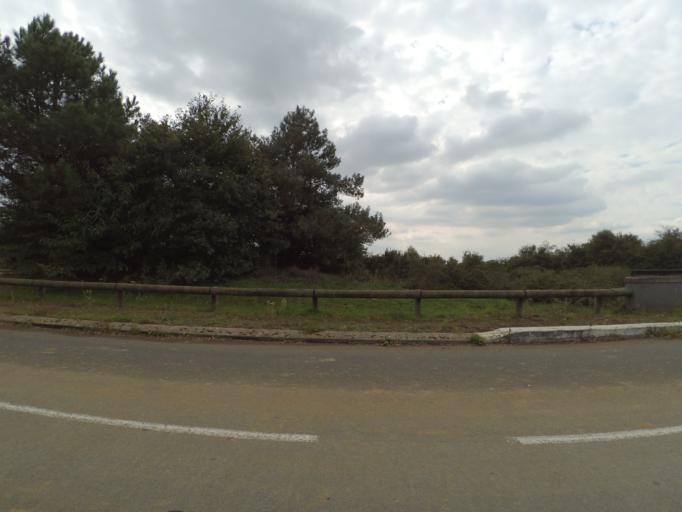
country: FR
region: Pays de la Loire
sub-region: Departement de la Vendee
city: Bouffere
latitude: 46.9843
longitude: -1.3543
